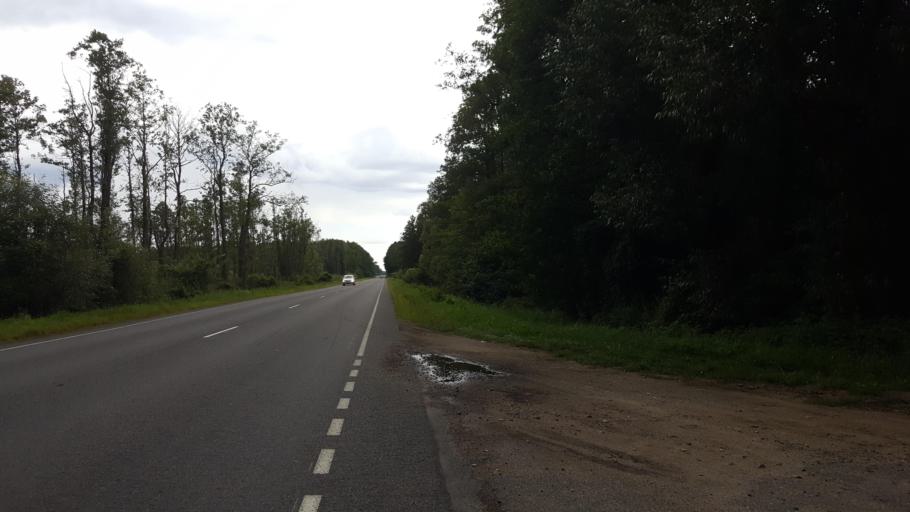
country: BY
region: Brest
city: Zhabinka
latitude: 52.2790
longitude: 23.9496
